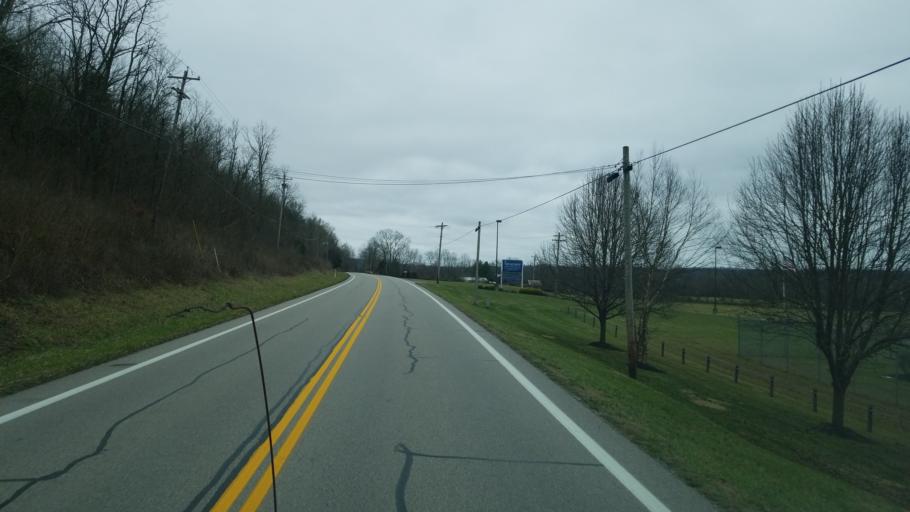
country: US
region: Ohio
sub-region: Clermont County
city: New Richmond
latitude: 38.8389
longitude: -84.2226
